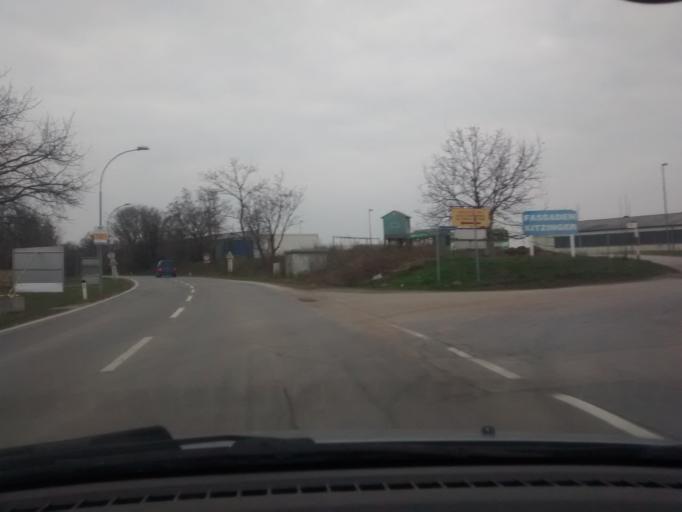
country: AT
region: Lower Austria
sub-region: Politischer Bezirk Wien-Umgebung
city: Fischamend Dorf
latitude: 48.1161
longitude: 16.6047
